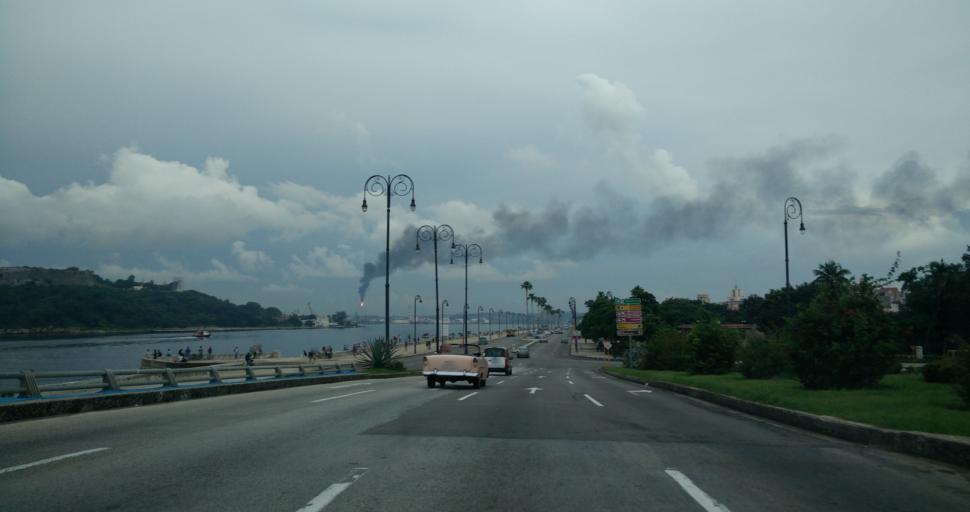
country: CU
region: La Habana
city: Centro Habana
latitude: 23.1449
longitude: -82.3547
